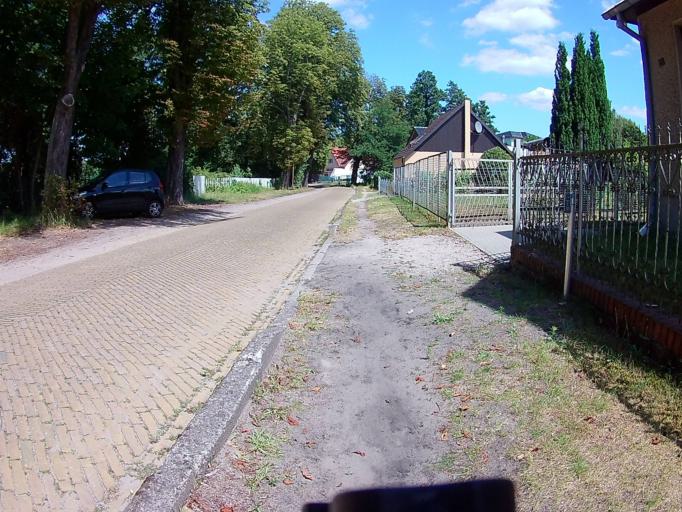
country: DE
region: Brandenburg
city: Gross Koris
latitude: 52.1633
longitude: 13.6570
